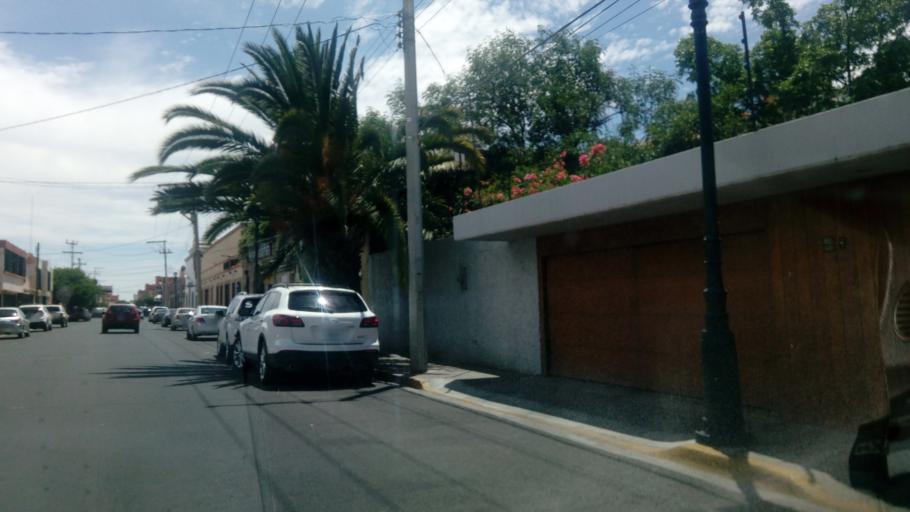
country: MX
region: Durango
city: Victoria de Durango
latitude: 24.0251
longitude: -104.6756
